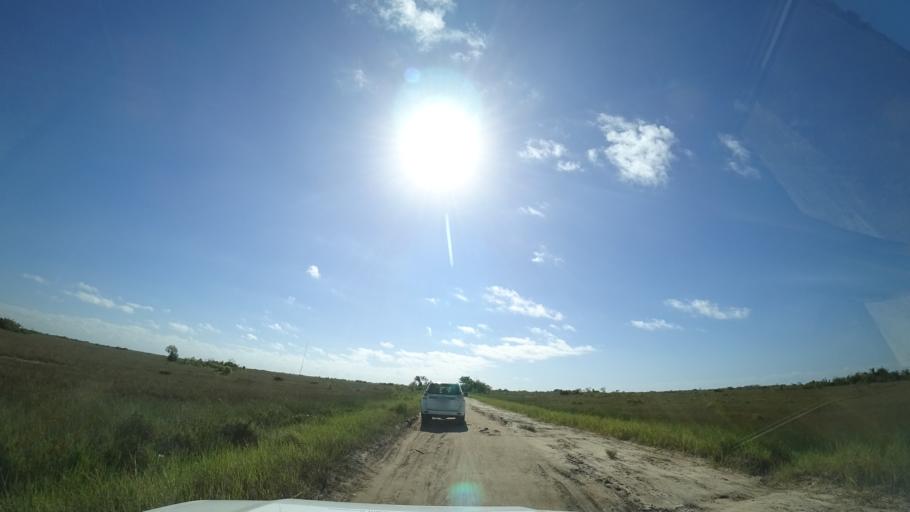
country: MZ
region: Sofala
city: Beira
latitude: -19.6996
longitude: 35.0280
